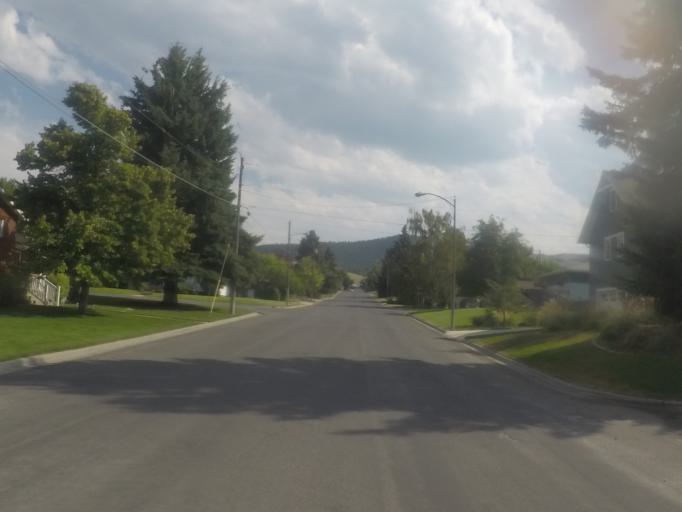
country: US
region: Montana
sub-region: Lewis and Clark County
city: Helena
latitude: 46.5864
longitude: -112.0072
